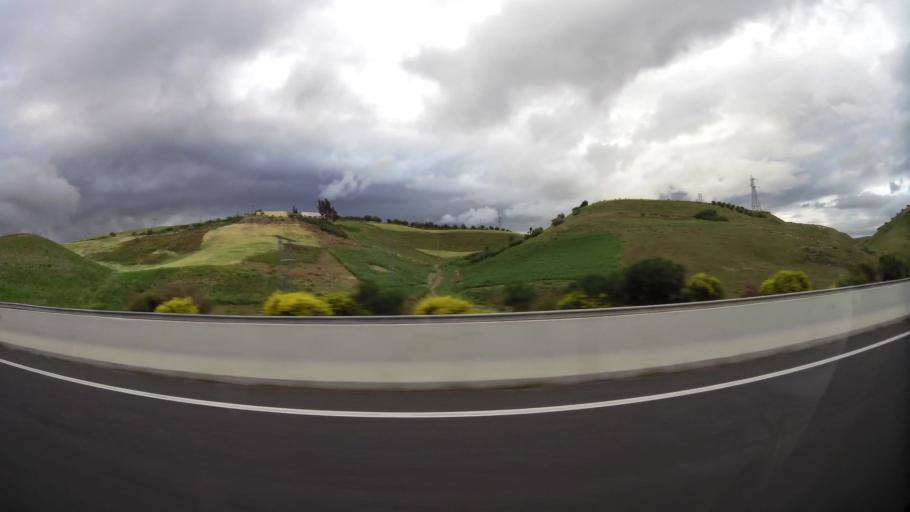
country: MA
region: Taza-Al Hoceima-Taounate
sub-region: Taza
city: Taza
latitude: 34.2606
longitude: -3.9466
